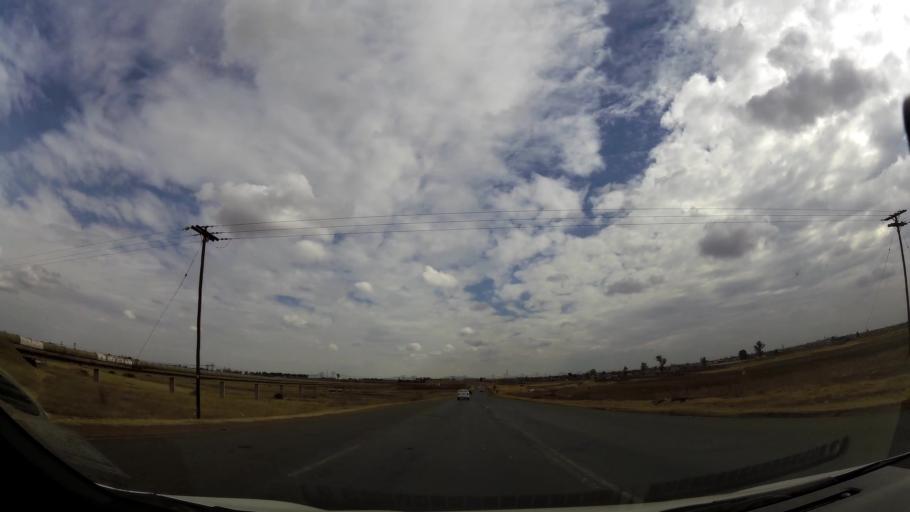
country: ZA
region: Gauteng
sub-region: Ekurhuleni Metropolitan Municipality
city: Germiston
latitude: -26.4269
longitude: 28.1676
